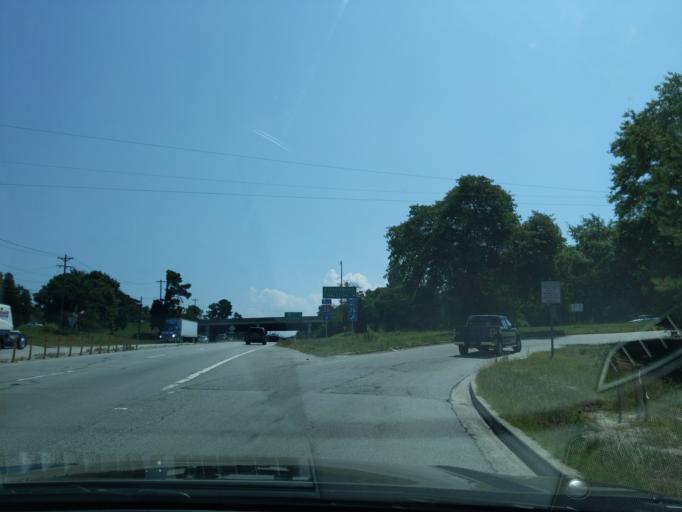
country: US
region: South Carolina
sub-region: Lexington County
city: Springdale
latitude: 33.9802
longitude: -81.1089
